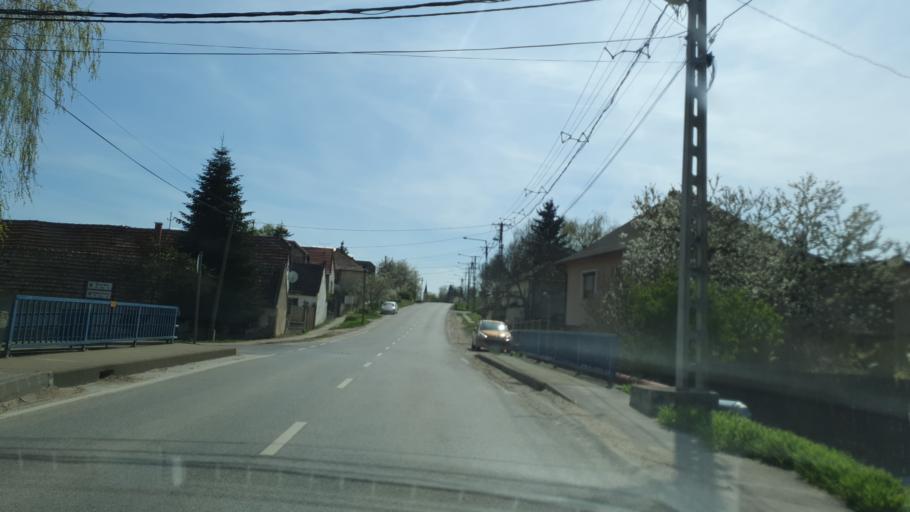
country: HU
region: Fejer
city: Pusztavam
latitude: 47.4370
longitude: 18.2326
